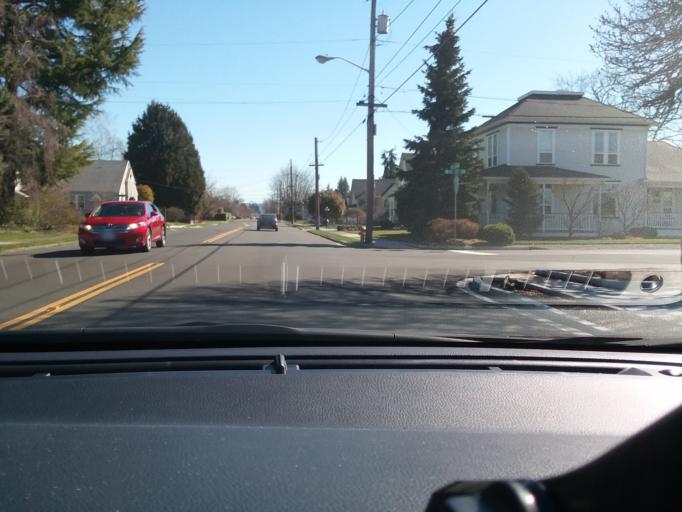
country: US
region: Washington
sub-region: Pierce County
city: Puyallup
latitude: 47.1903
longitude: -122.3073
